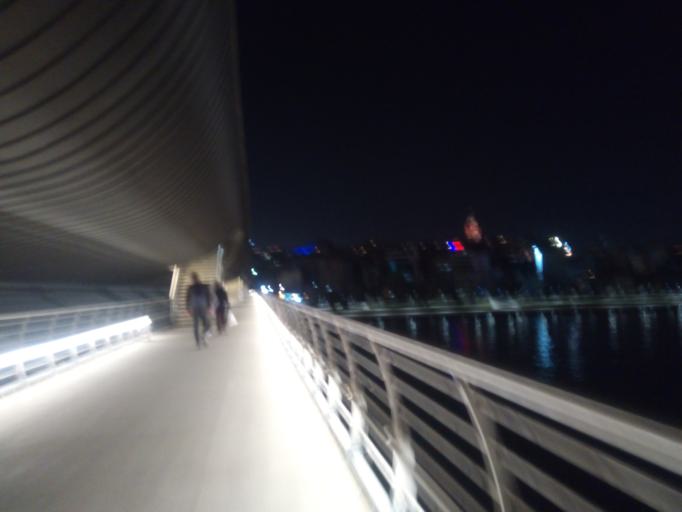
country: TR
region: Istanbul
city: Eminoenue
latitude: 41.0221
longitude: 28.9663
